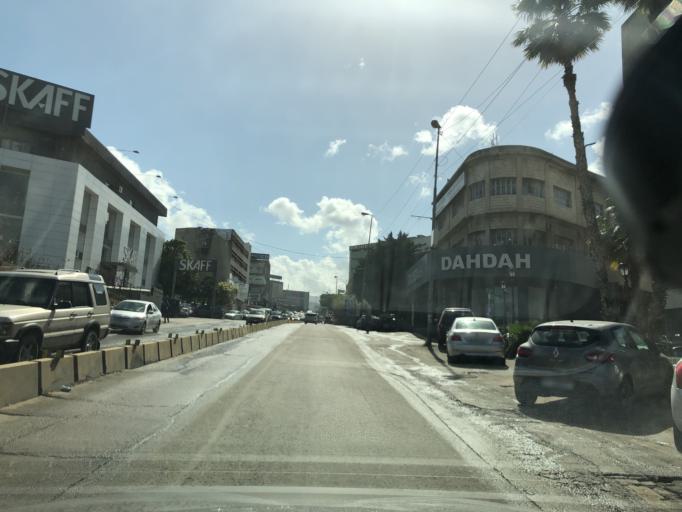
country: LB
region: Mont-Liban
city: Jdaidet el Matn
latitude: 33.8665
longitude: 35.5451
